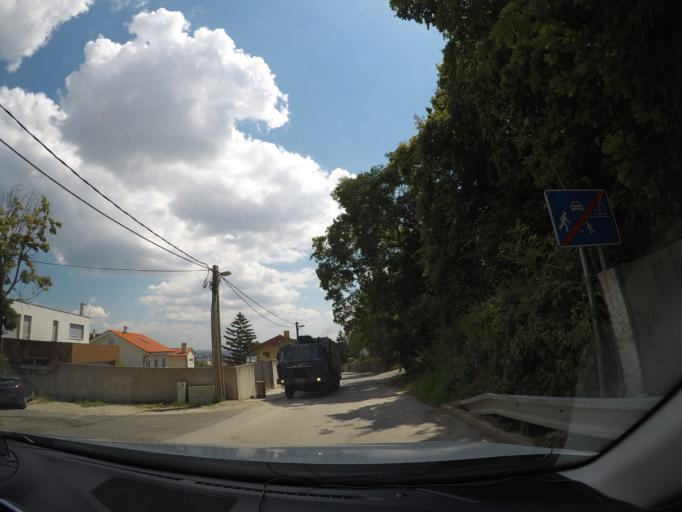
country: SK
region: Bratislavsky
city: Bratislava
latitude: 48.1773
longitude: 17.1126
